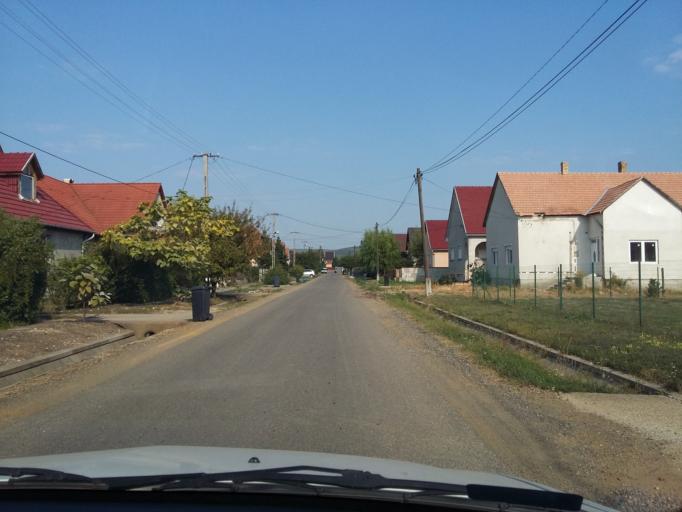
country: HU
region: Borsod-Abauj-Zemplen
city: Bekecs
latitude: 48.1522
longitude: 21.1871
